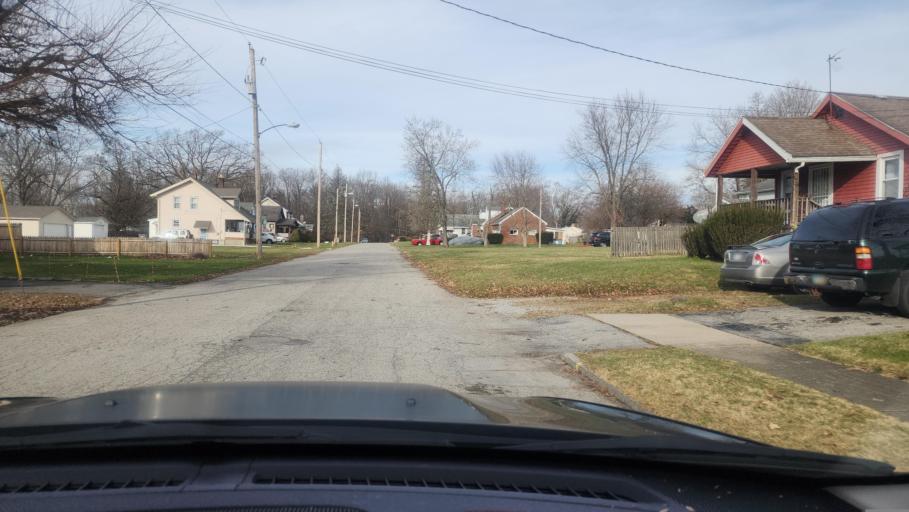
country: US
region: Ohio
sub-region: Mahoning County
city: Campbell
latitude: 41.1056
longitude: -80.6173
